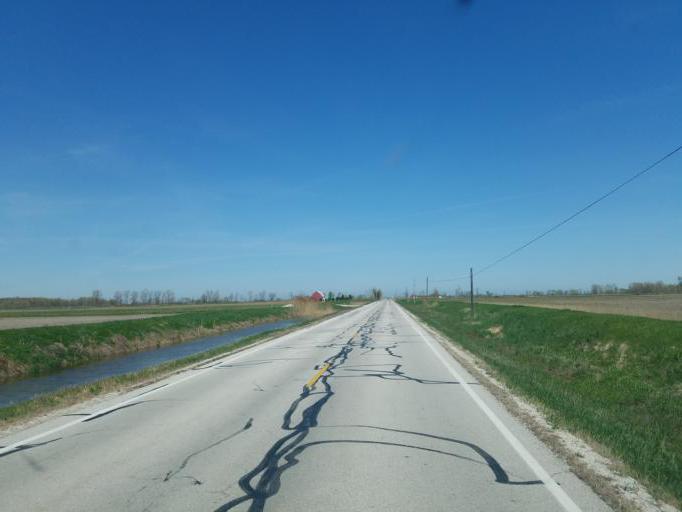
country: US
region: Ohio
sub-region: Ottawa County
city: Oak Harbor
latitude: 41.5966
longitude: -83.1451
